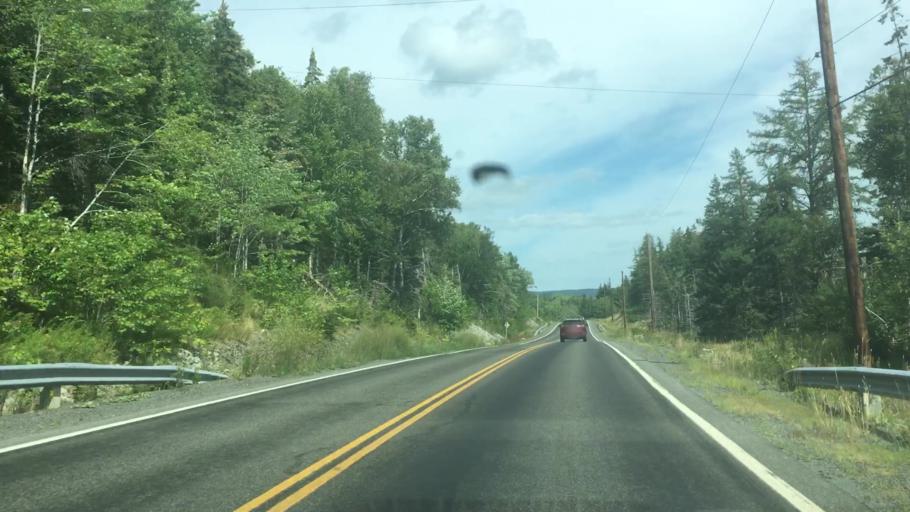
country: CA
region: Nova Scotia
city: Sydney Mines
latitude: 46.2150
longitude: -60.6201
